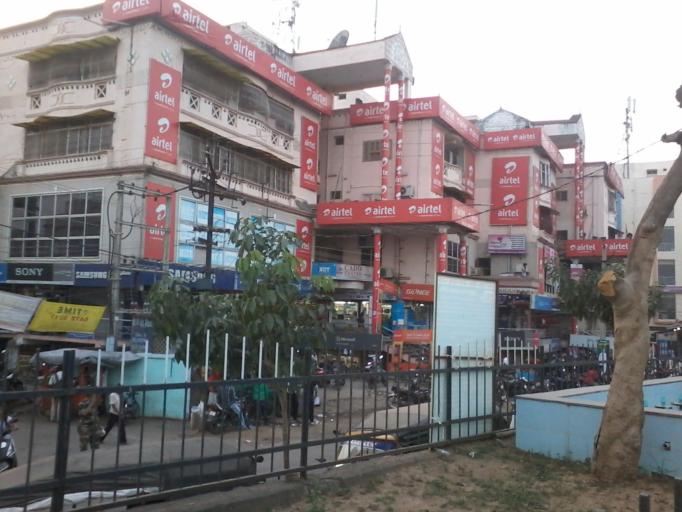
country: IN
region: Odisha
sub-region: Ganjam
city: Brahmapur
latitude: 19.3099
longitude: 84.7896
